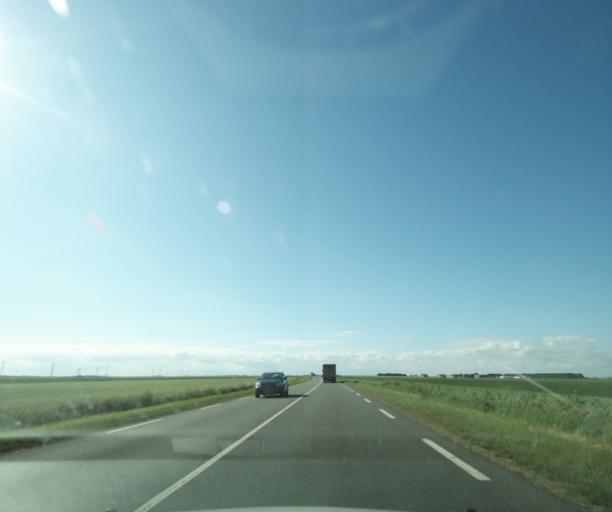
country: FR
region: Centre
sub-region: Departement d'Eure-et-Loir
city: Janville
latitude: 48.2320
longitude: 1.7912
